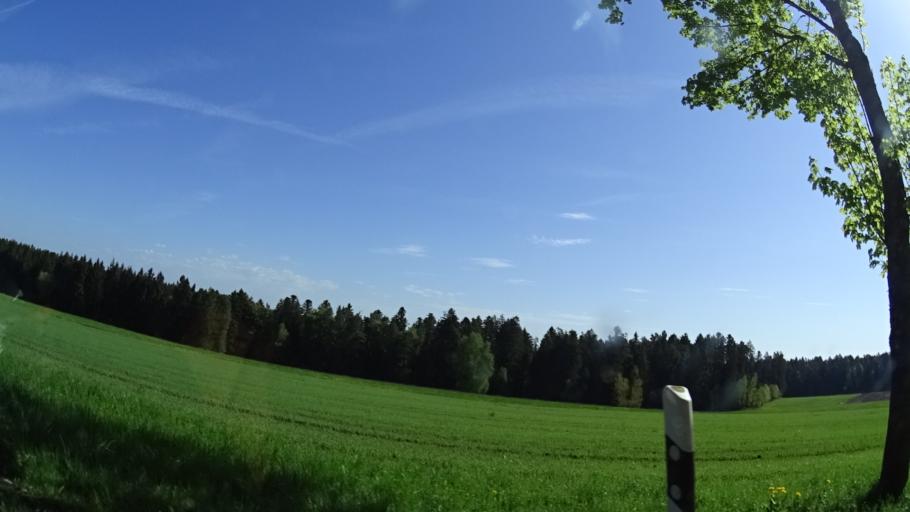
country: DE
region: Baden-Wuerttemberg
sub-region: Karlsruhe Region
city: Neuweiler
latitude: 48.6409
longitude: 8.5790
